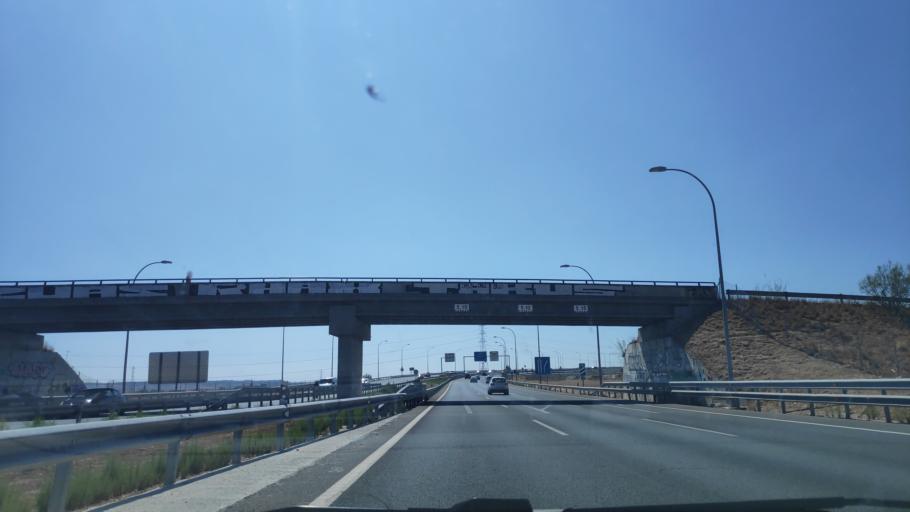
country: ES
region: Madrid
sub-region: Provincia de Madrid
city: Torrejon de la Calzada
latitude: 40.2022
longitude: -3.7896
